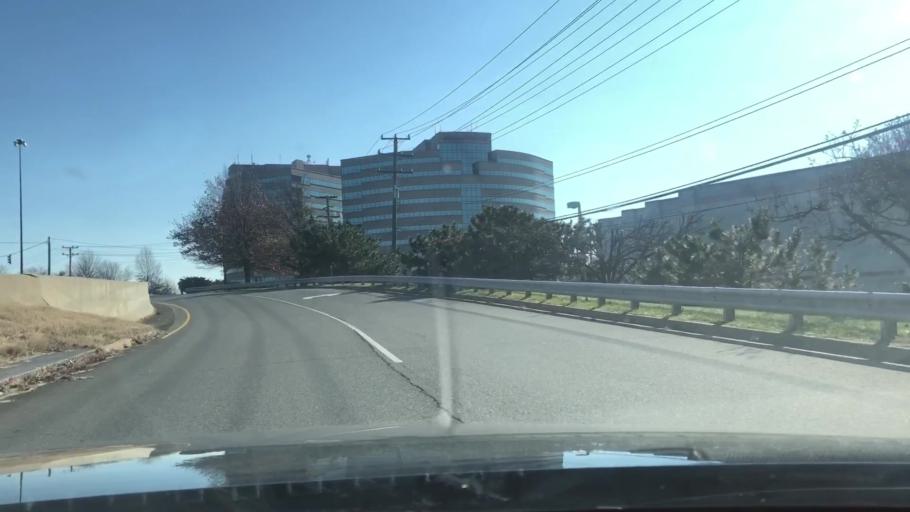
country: US
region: Virginia
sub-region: Fairfax County
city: Greenbriar
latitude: 38.8682
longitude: -77.3663
